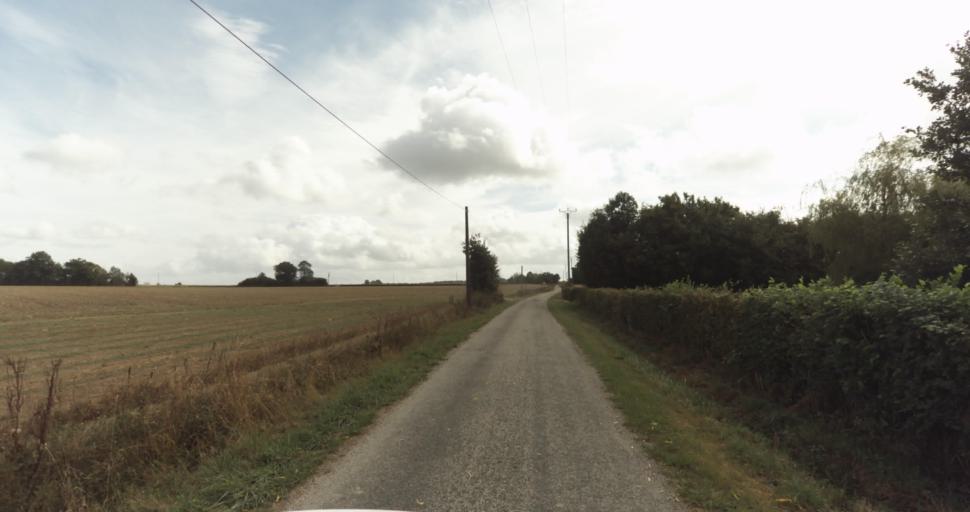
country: FR
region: Lower Normandy
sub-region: Departement de l'Orne
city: Gace
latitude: 48.8115
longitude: 0.3817
